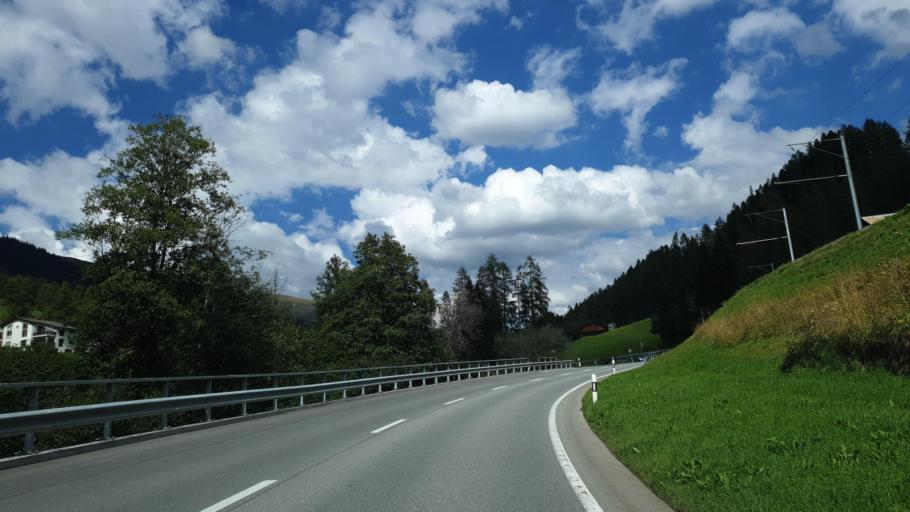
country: CH
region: Grisons
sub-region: Praettigau/Davos District
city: Davos
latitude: 46.7386
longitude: 9.7764
